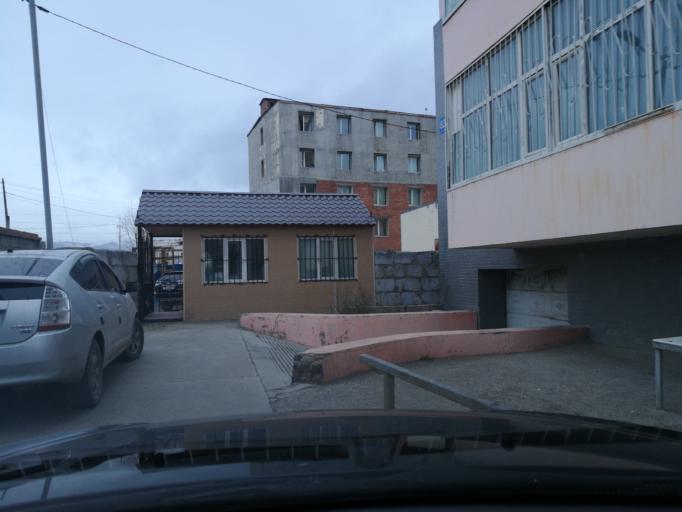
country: MN
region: Ulaanbaatar
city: Ulaanbaatar
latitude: 47.9294
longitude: 106.9123
